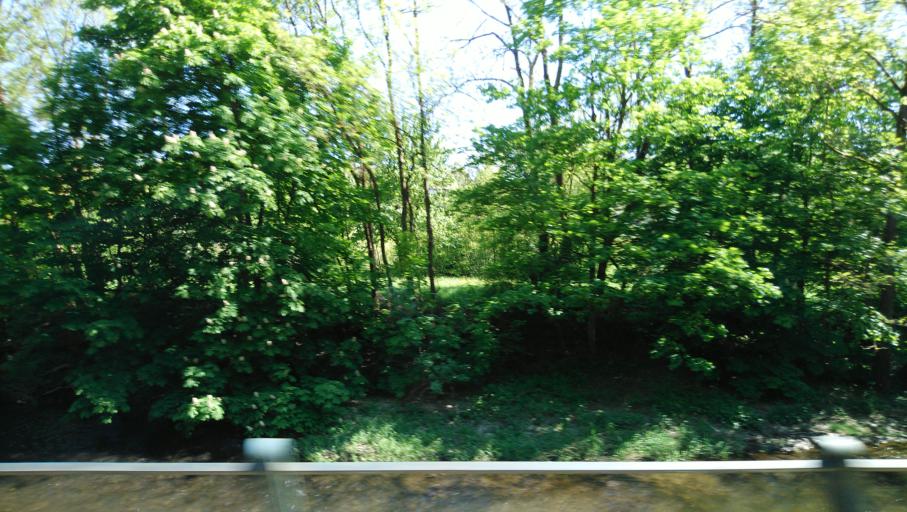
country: LU
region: Diekirch
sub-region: Canton de Vianden
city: Vianden
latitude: 49.9228
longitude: 6.2182
